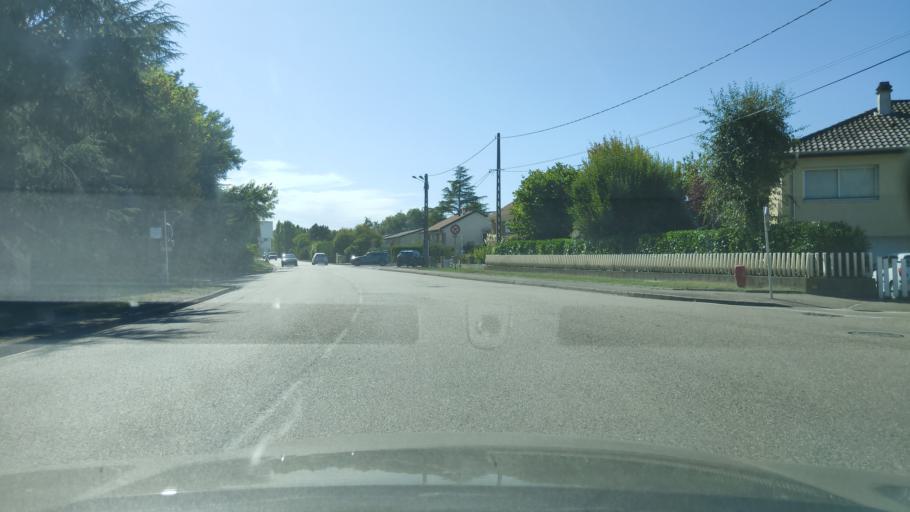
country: FR
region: Lorraine
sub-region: Departement de la Moselle
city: Moulins-les-Metz
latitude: 49.1011
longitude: 6.1080
